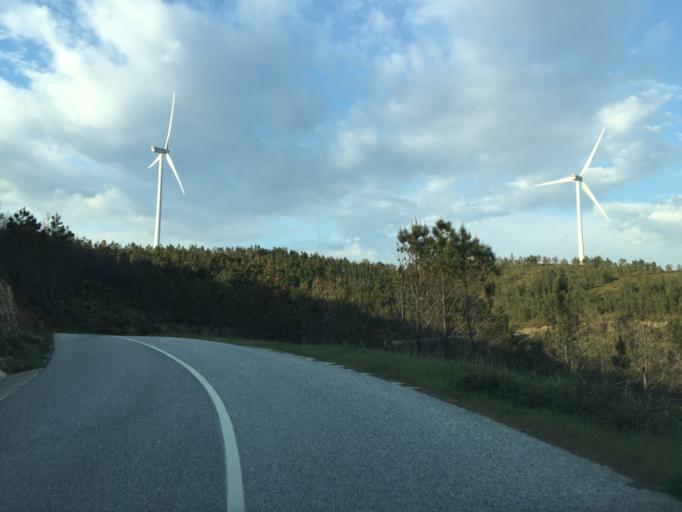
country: PT
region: Coimbra
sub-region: Pampilhosa da Serra
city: Pampilhosa da Serra
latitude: 40.1109
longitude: -8.0005
